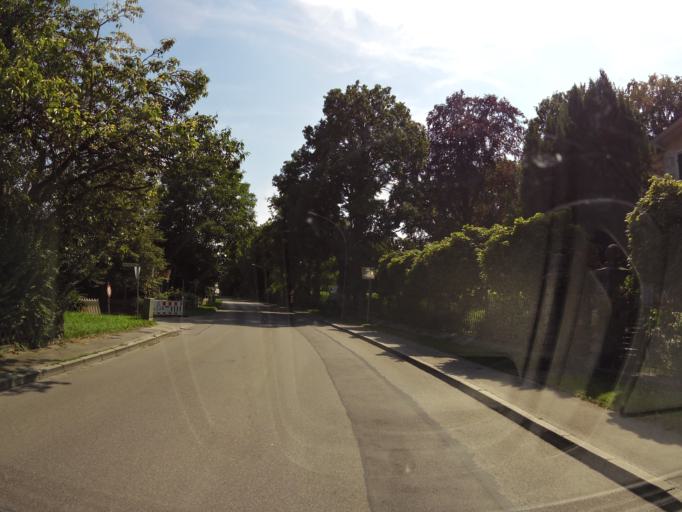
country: DE
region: Bavaria
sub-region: Upper Bavaria
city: Diessen am Ammersee
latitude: 47.9429
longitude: 11.1047
